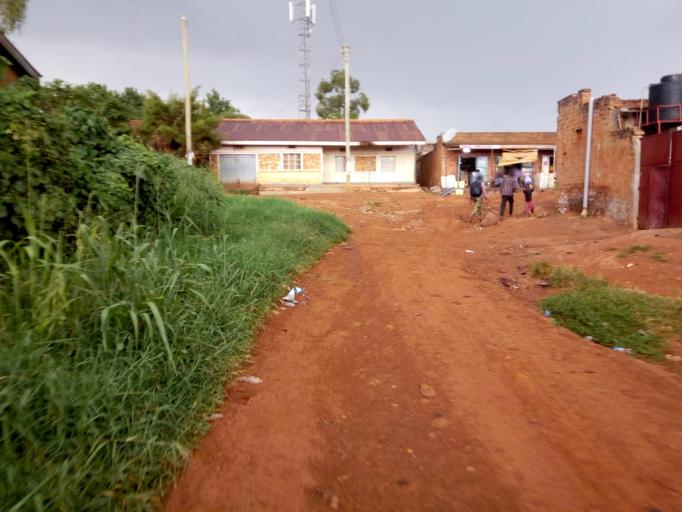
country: UG
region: Western Region
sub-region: Masindi District
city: Masindi
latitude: 1.6815
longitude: 31.7180
